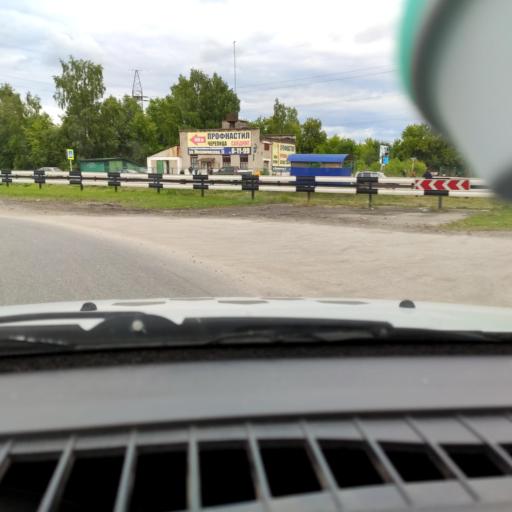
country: RU
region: Perm
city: Chusovoy
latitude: 58.2913
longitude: 57.8174
